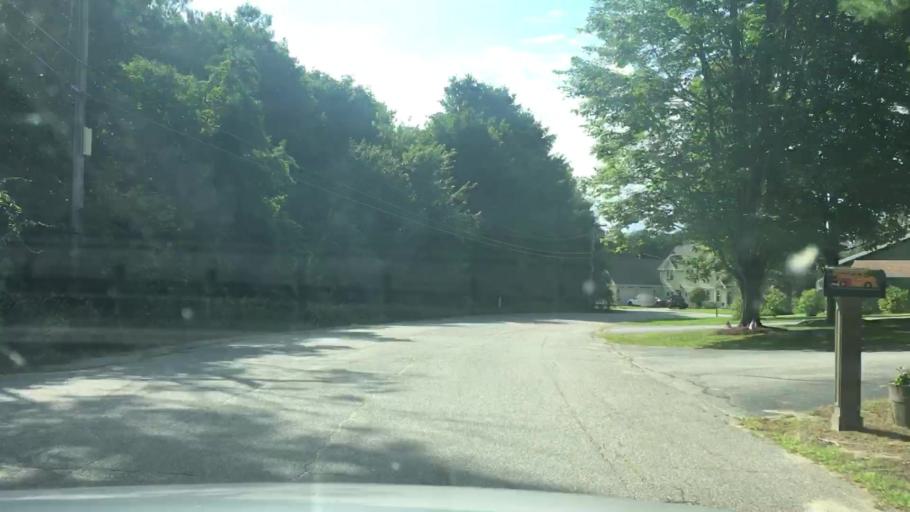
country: US
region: Maine
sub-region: Androscoggin County
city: Lewiston
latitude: 44.1161
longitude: -70.2025
